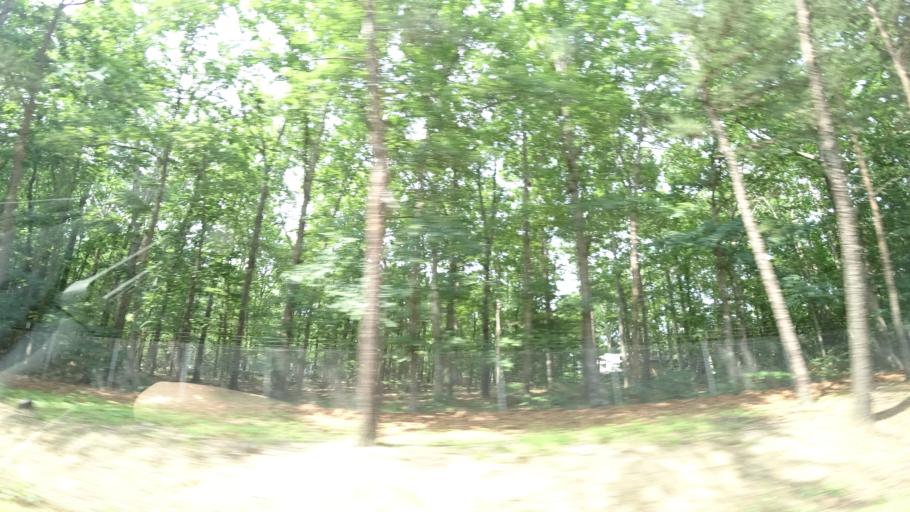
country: US
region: Virginia
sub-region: Spotsylvania County
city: Spotsylvania Courthouse
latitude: 38.1389
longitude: -77.5482
